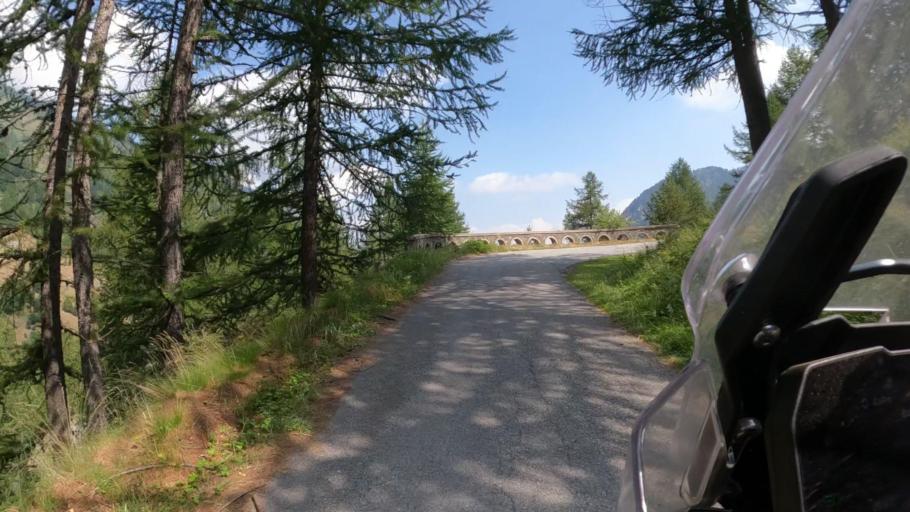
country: IT
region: Piedmont
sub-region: Provincia di Cuneo
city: Marmora
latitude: 44.4204
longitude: 7.1031
